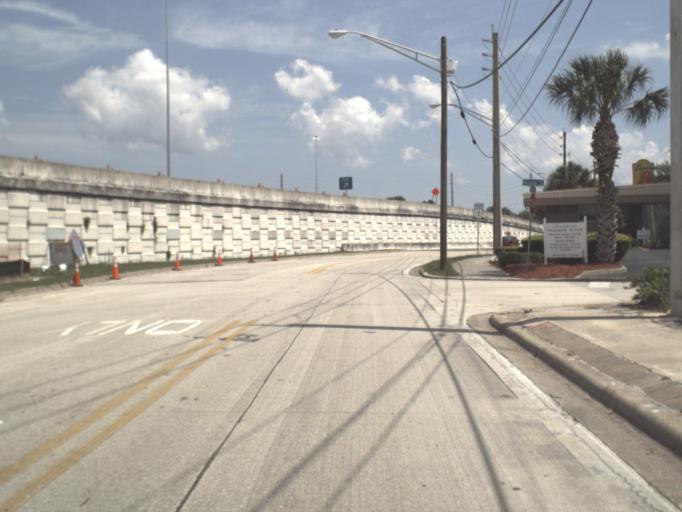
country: US
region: Florida
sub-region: Duval County
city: Jacksonville
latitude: 30.3075
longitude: -81.6467
